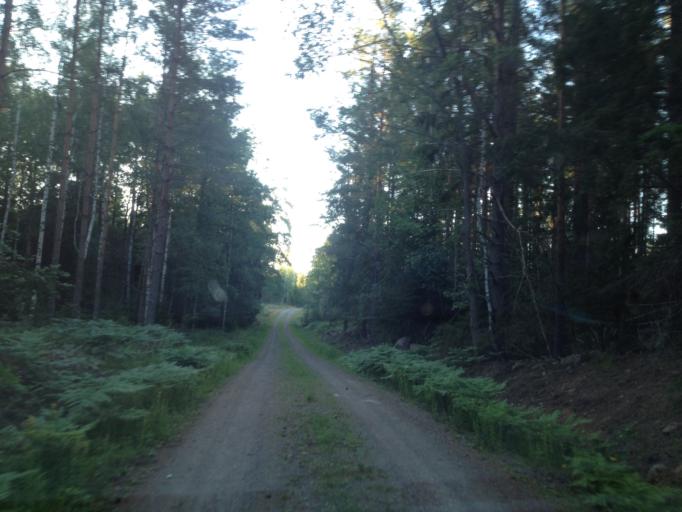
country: SE
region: Kalmar
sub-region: Vasterviks Kommun
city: Overum
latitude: 57.9938
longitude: 16.1696
